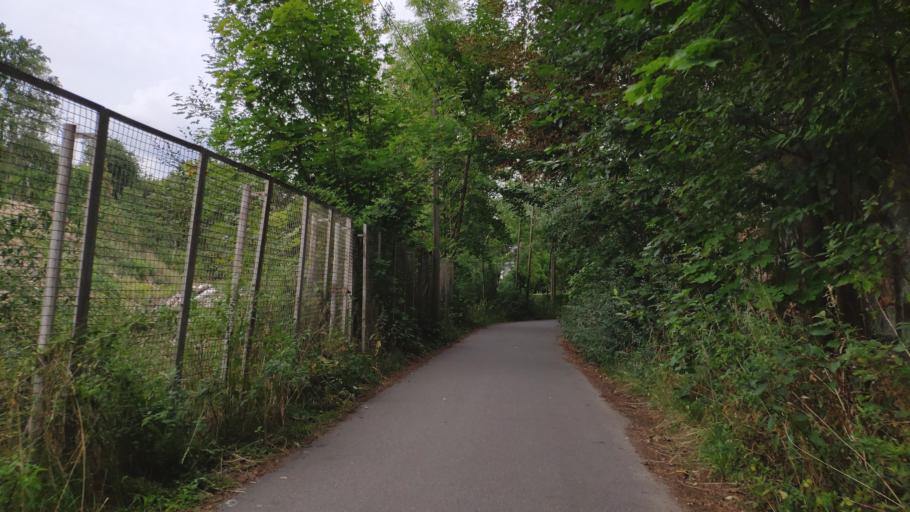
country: DE
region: Saxony
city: Chemnitz
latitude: 50.8233
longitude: 12.8877
